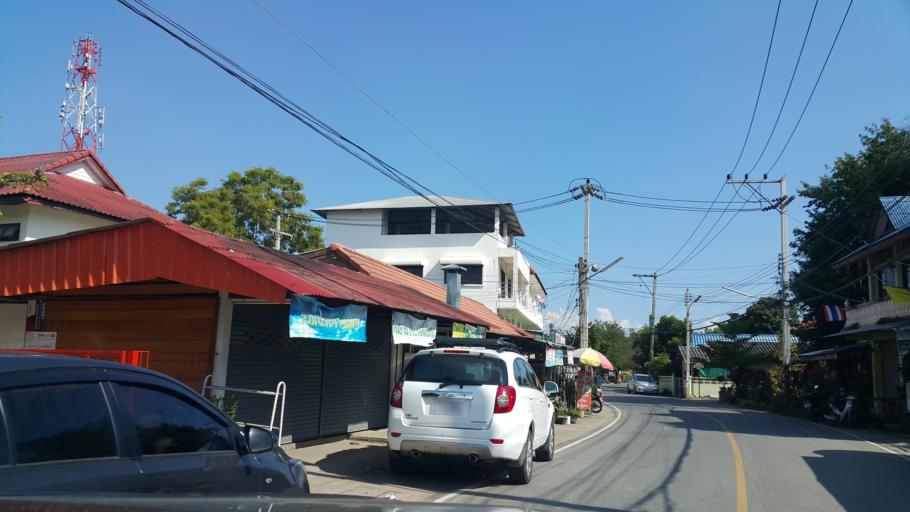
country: TH
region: Chiang Mai
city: Hang Dong
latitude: 18.7343
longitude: 98.9559
